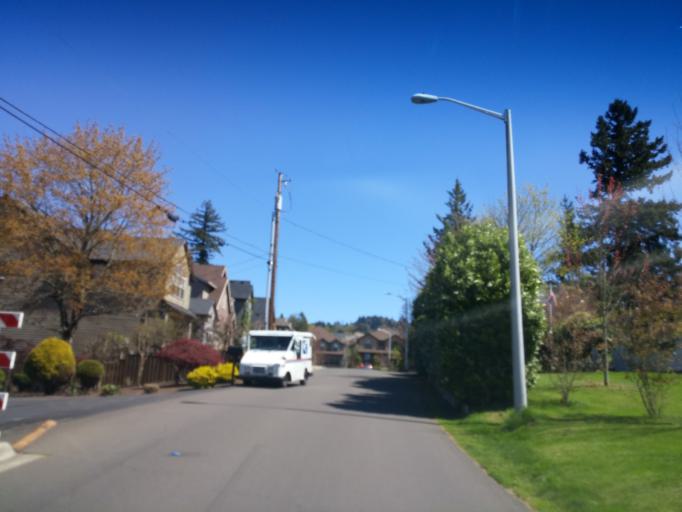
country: US
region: Oregon
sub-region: Washington County
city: West Haven
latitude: 45.5282
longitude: -122.7814
